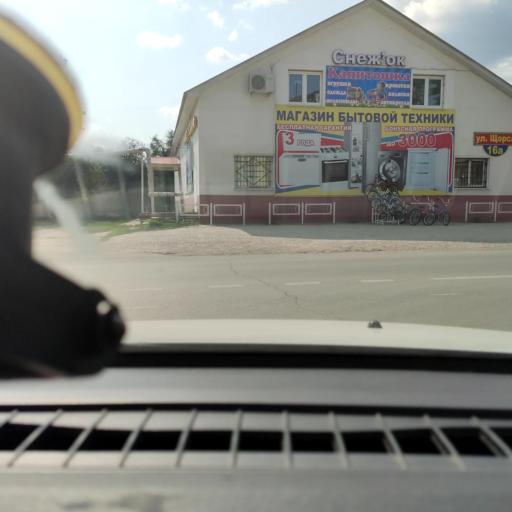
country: RU
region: Samara
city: Chapayevsk
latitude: 52.9528
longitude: 49.6874
